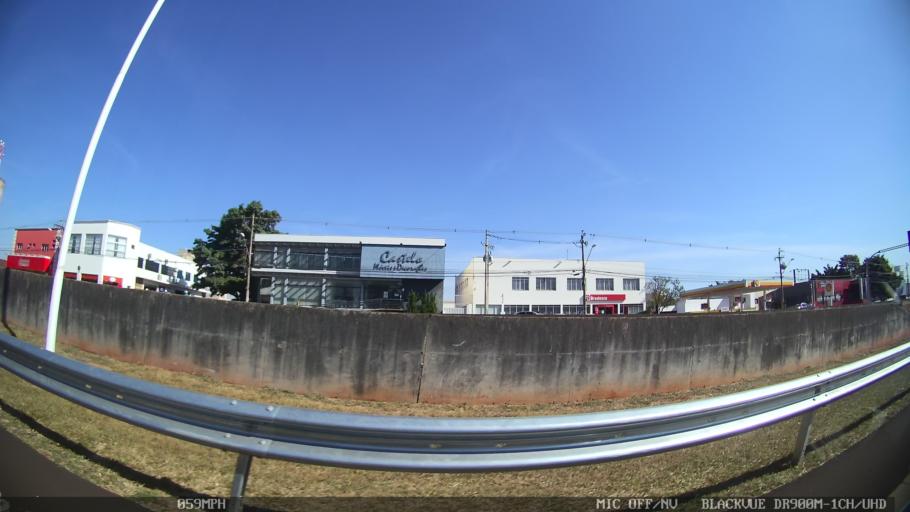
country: BR
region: Sao Paulo
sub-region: Ribeirao Preto
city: Ribeirao Preto
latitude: -21.1956
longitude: -47.7730
